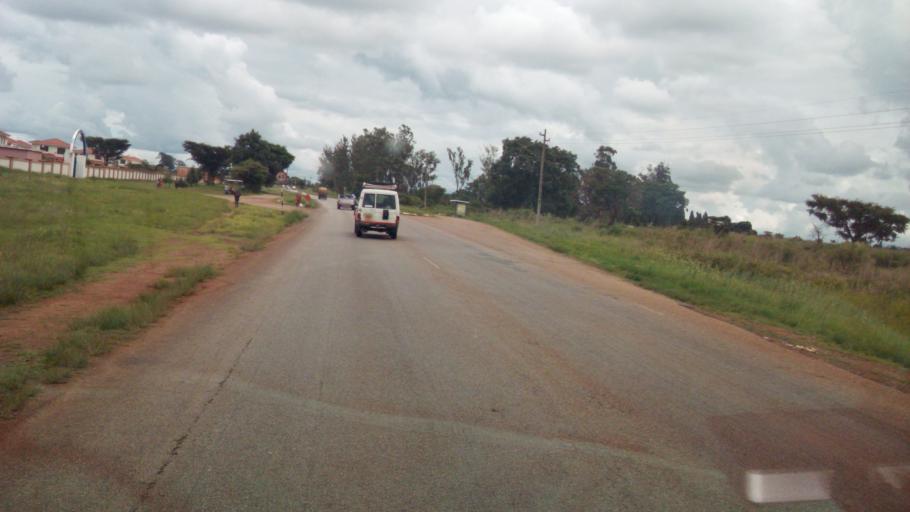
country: ZW
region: Harare
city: Harare
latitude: -17.7369
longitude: 31.0249
